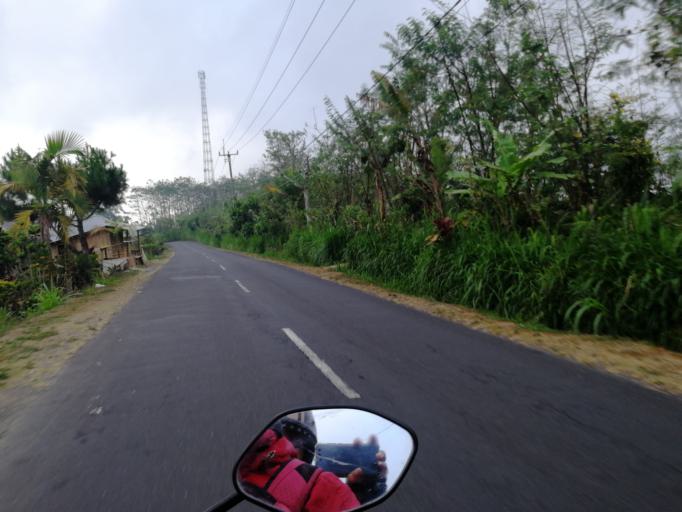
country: ID
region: Bali
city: Banjar Ambengan
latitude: -8.2403
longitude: 115.2421
